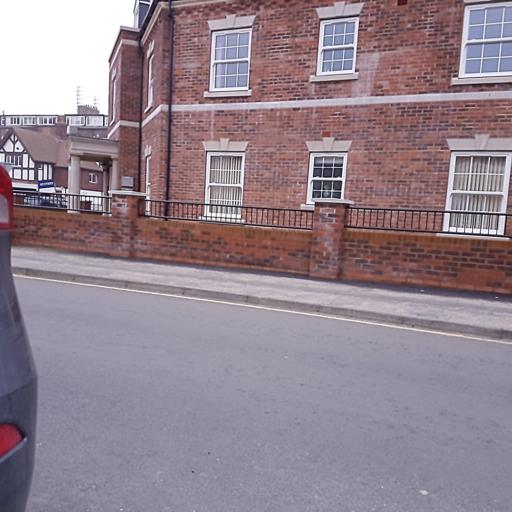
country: GB
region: England
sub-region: North Yorkshire
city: Filey
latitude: 54.2060
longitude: -0.2880
